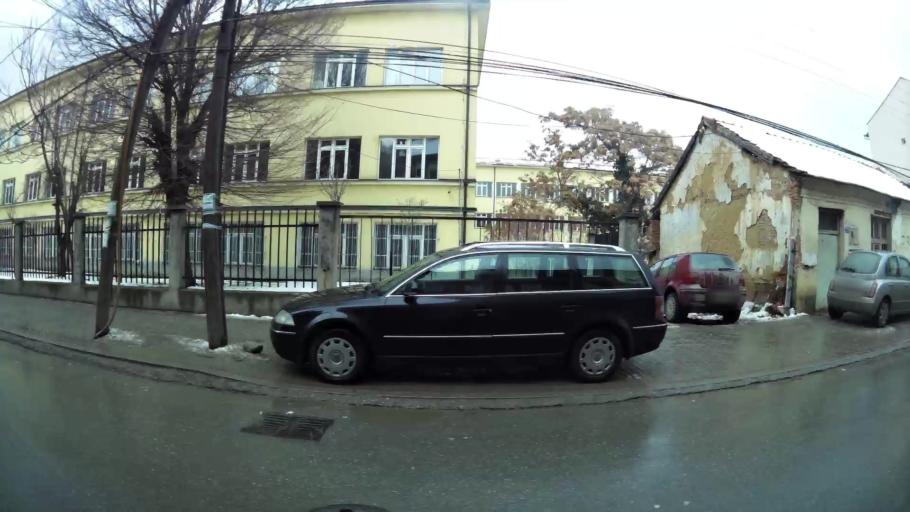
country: XK
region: Pristina
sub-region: Komuna e Prishtines
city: Pristina
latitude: 42.6681
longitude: 21.1692
